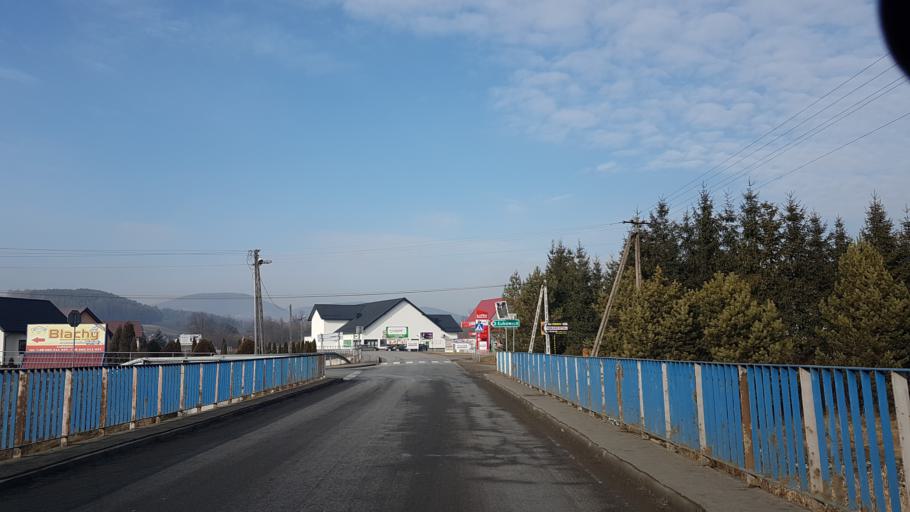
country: PL
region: Lesser Poland Voivodeship
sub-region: Powiat nowosadecki
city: Olszana
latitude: 49.5943
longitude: 20.5345
